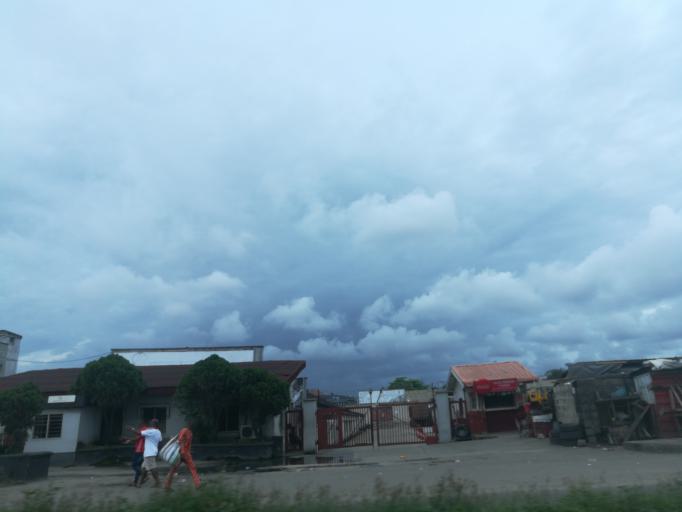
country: NG
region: Lagos
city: Ebute Metta
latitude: 6.4743
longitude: 3.3820
